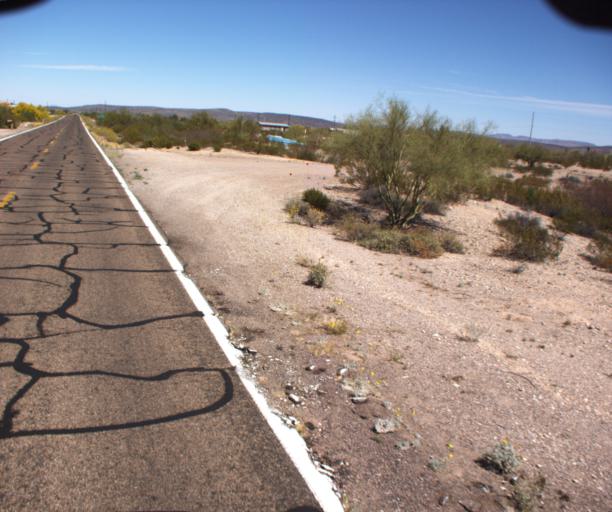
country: US
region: Arizona
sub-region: Pima County
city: Ajo
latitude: 32.4198
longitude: -112.8715
